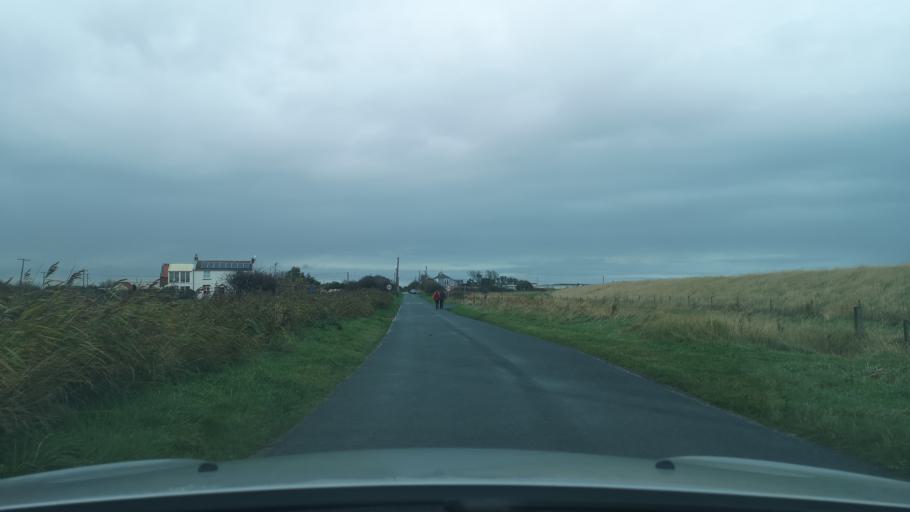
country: GB
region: England
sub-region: East Riding of Yorkshire
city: Easington
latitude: 53.6179
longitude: 0.1400
